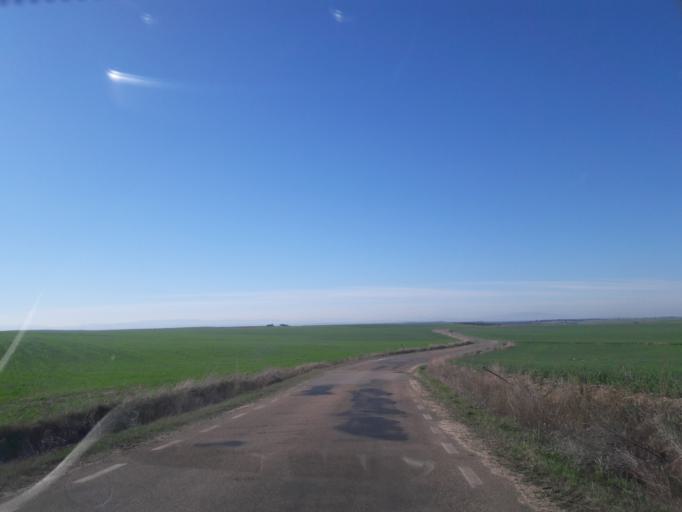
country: ES
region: Castille and Leon
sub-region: Provincia de Salamanca
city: Tordillos
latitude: 40.8751
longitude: -5.3294
